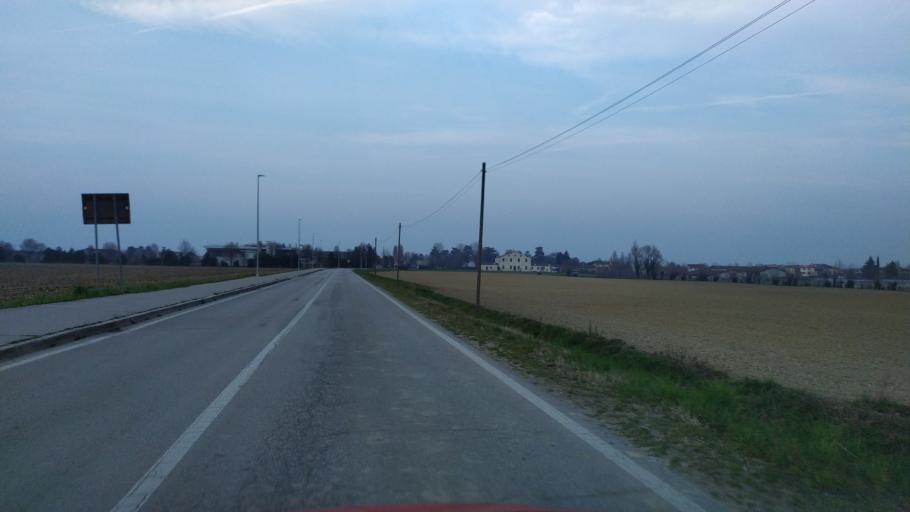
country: IT
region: Veneto
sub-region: Provincia di Vicenza
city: Vigardolo
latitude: 45.6027
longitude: 11.5826
